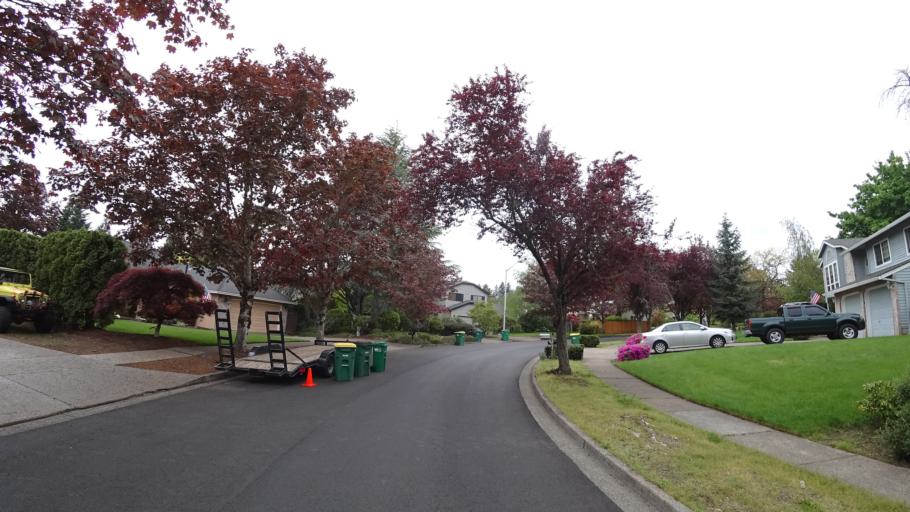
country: US
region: Oregon
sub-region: Washington County
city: Beaverton
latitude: 45.4552
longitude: -122.8235
